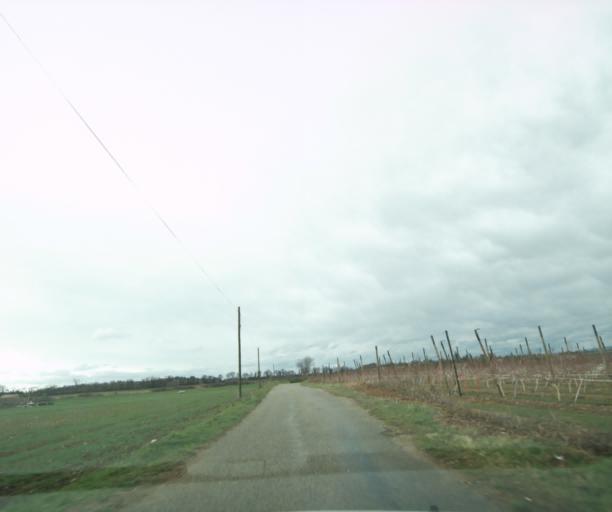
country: FR
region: Rhone-Alpes
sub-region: Departement de la Drome
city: Bourg-les-Valence
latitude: 44.9643
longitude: 4.9253
